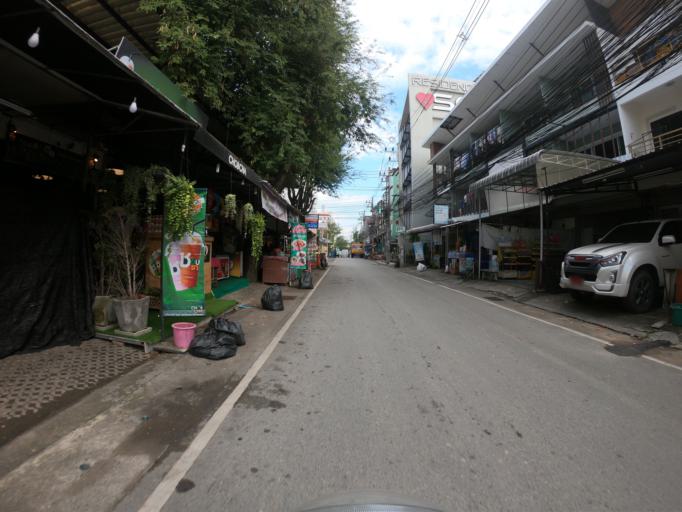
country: TH
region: Chiang Mai
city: Chiang Mai
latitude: 18.8086
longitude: 98.9678
